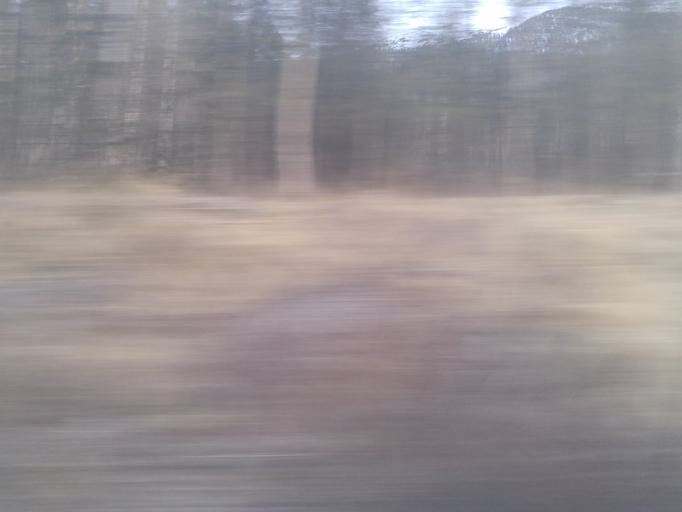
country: NO
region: Oppland
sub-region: Dovre
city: Dovre
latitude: 61.8943
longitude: 9.3982
